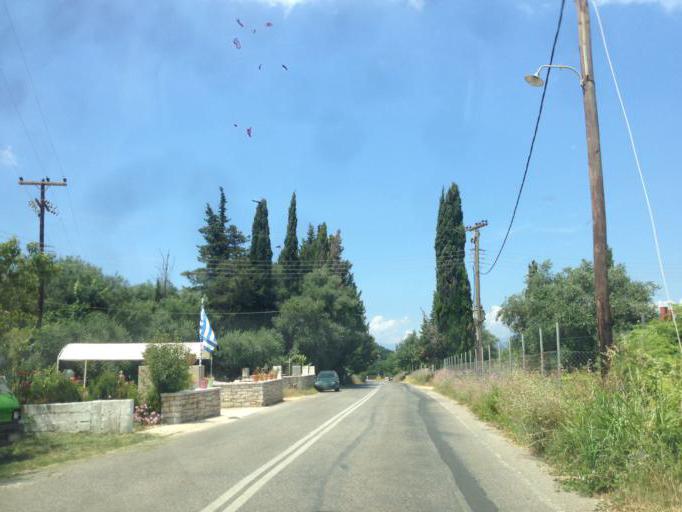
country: GR
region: Ionian Islands
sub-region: Nomos Kerkyras
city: Acharavi
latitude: 39.7799
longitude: 19.9247
